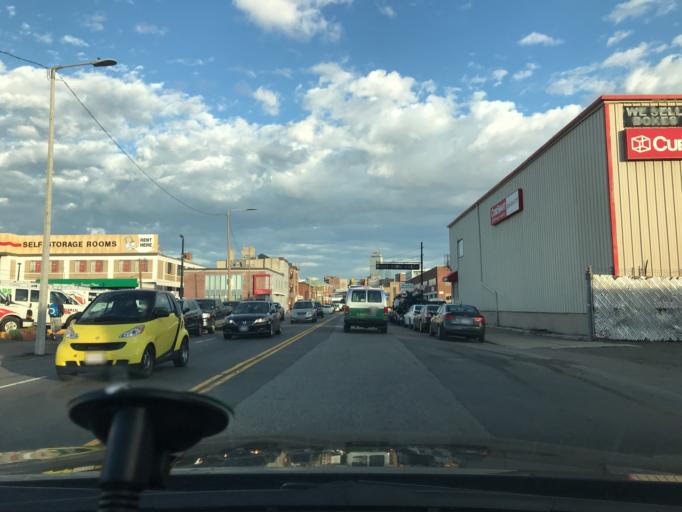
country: US
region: Massachusetts
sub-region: Suffolk County
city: South Boston
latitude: 42.3285
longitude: -71.0683
